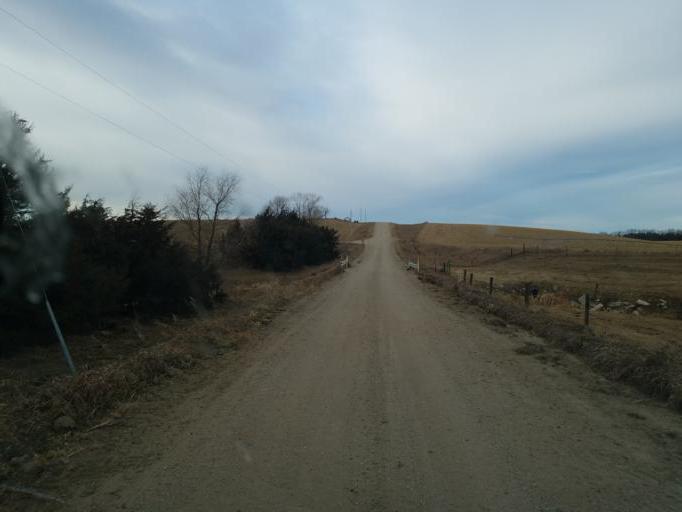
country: US
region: Nebraska
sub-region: Knox County
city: Bloomfield
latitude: 42.5576
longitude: -97.7433
